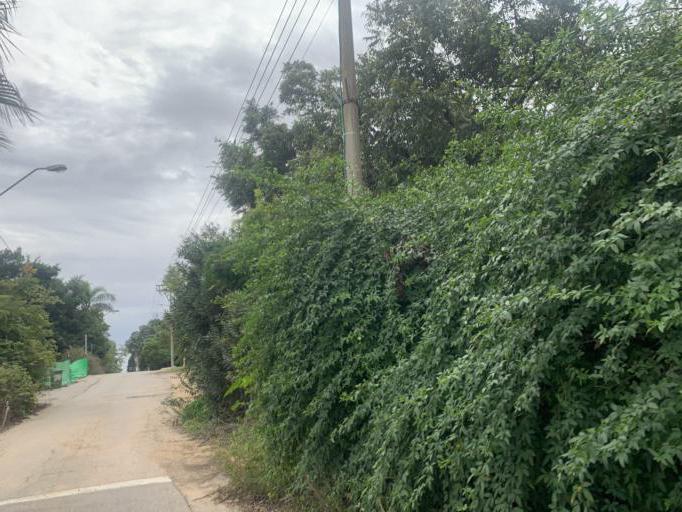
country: IL
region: Central District
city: Hod HaSharon
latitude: 32.1691
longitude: 34.8913
